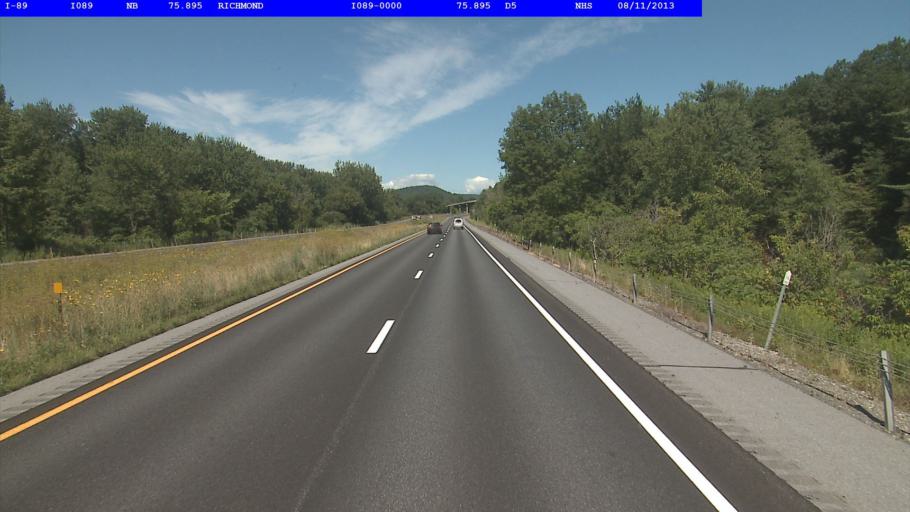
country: US
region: Vermont
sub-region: Chittenden County
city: Williston
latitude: 44.3988
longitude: -72.9783
